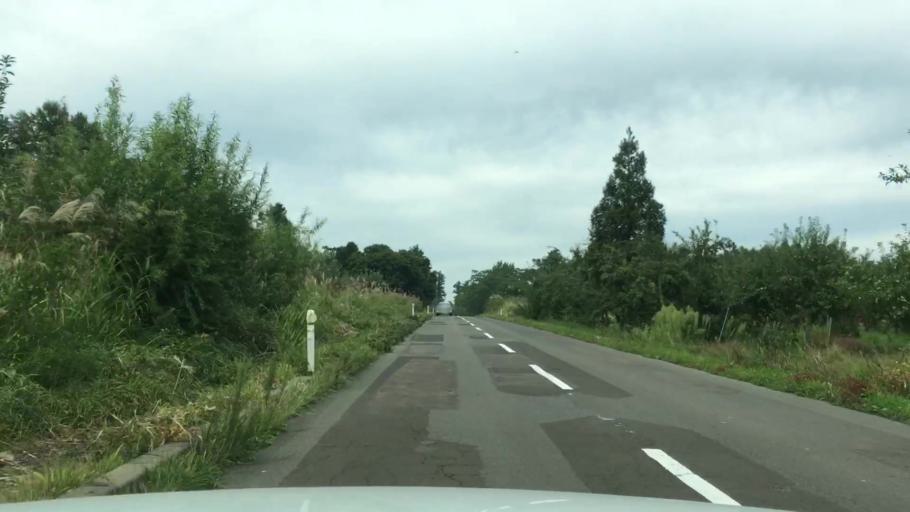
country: JP
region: Aomori
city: Hirosaki
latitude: 40.6752
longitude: 140.3829
